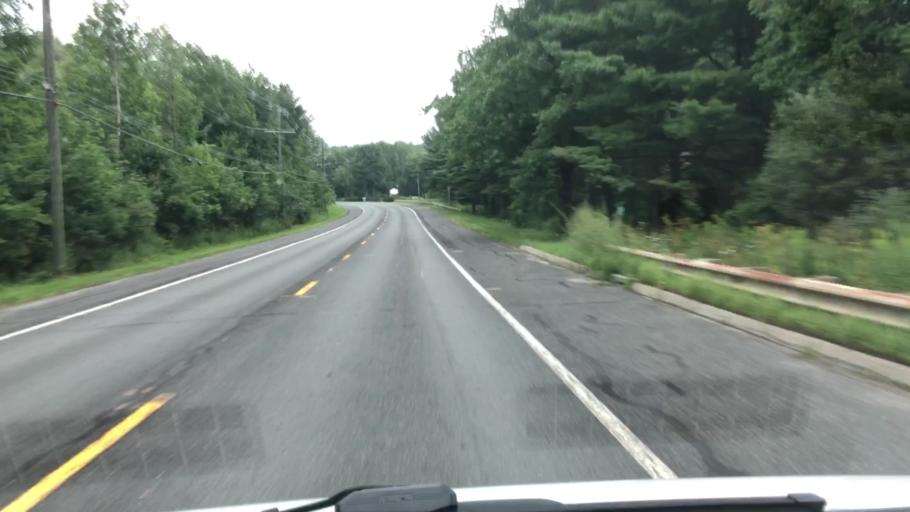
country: US
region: Massachusetts
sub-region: Berkshire County
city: Lanesborough
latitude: 42.5438
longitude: -73.2317
